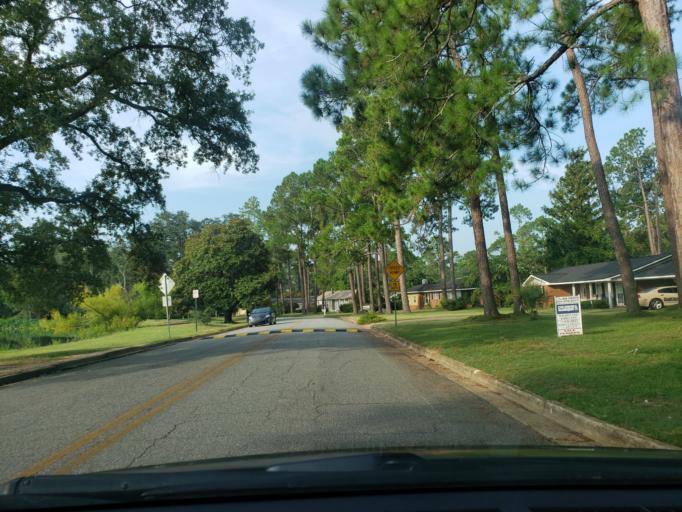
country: US
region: Georgia
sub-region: Dougherty County
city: Albany
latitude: 31.5984
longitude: -84.2036
